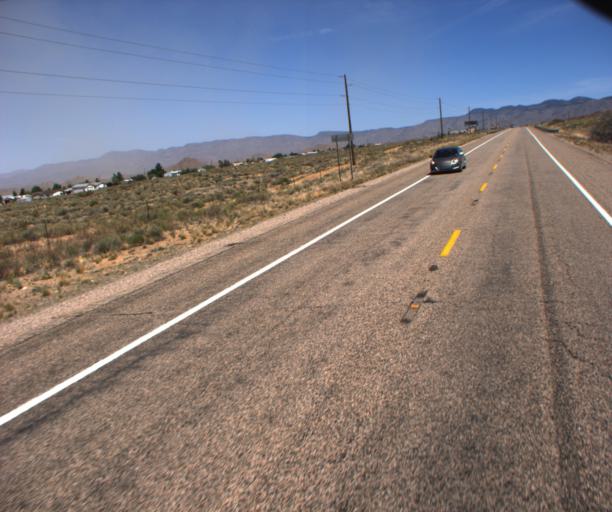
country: US
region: Arizona
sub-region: Mohave County
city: New Kingman-Butler
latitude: 35.3903
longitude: -113.8450
